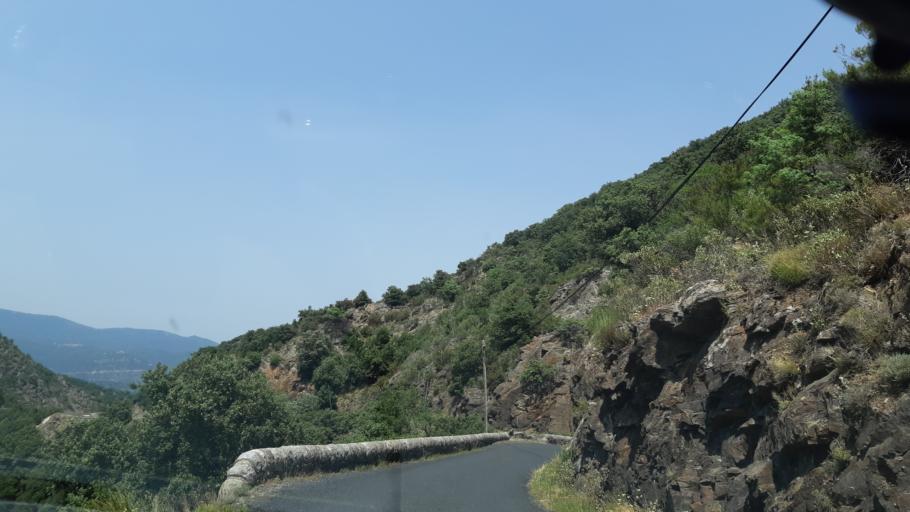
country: FR
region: Languedoc-Roussillon
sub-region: Departement des Pyrenees-Orientales
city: Vinca
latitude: 42.5987
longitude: 2.5131
